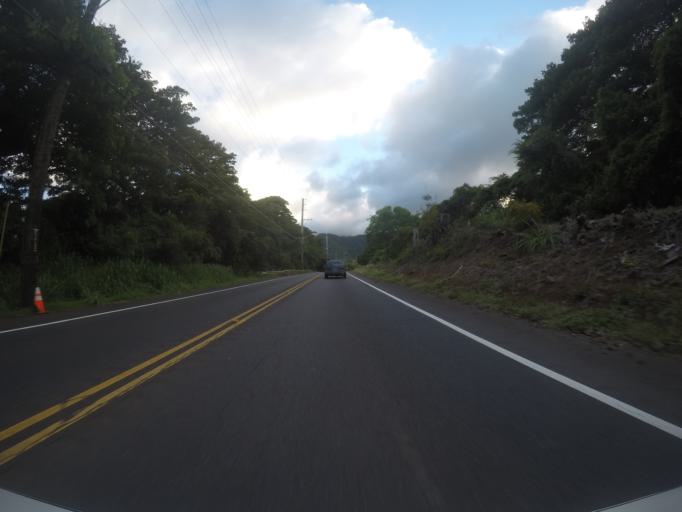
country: US
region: Hawaii
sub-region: Honolulu County
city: Ka'a'awa
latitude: 21.5134
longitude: -157.8475
